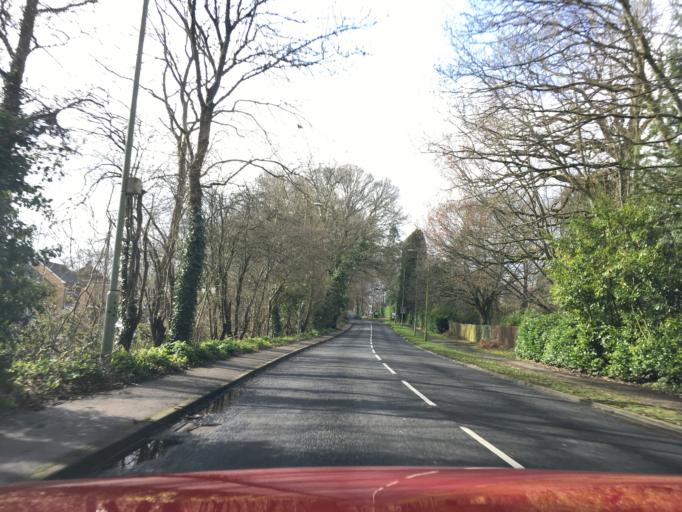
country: GB
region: England
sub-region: Hampshire
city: Chandlers Ford
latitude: 50.9913
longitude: -1.3685
